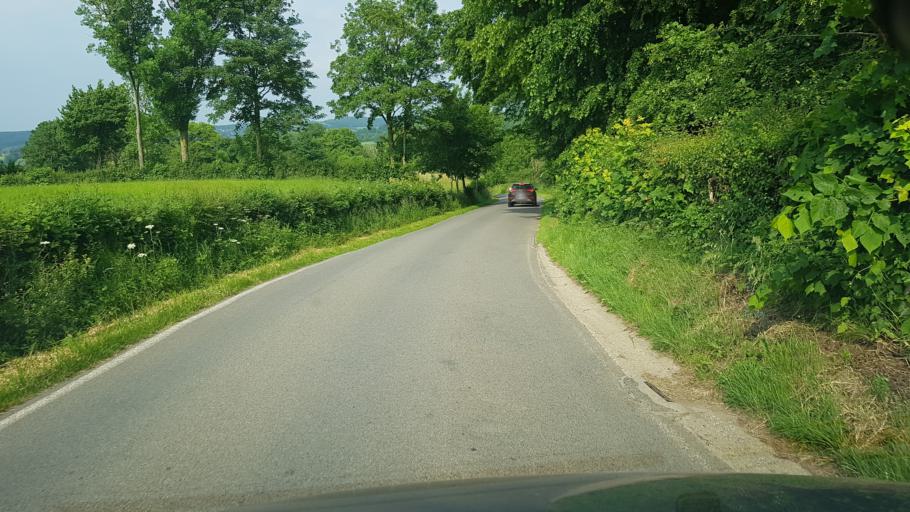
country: BE
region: Wallonia
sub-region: Province de Liege
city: Theux
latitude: 50.5278
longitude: 5.8072
